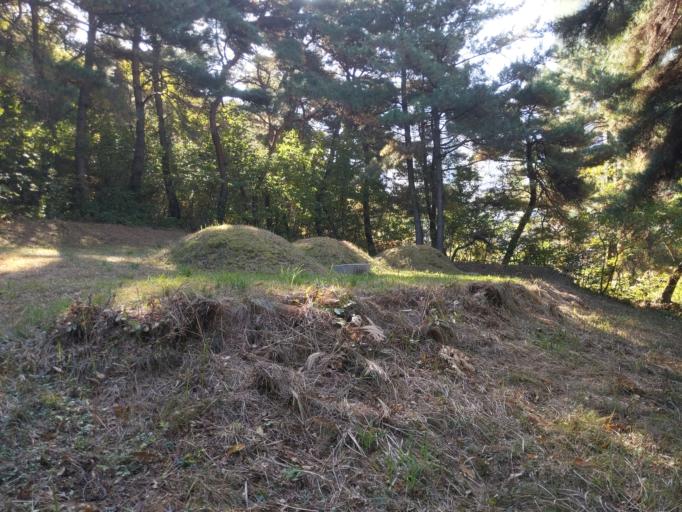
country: KR
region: Daegu
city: Hwawon
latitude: 35.7996
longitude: 128.5327
